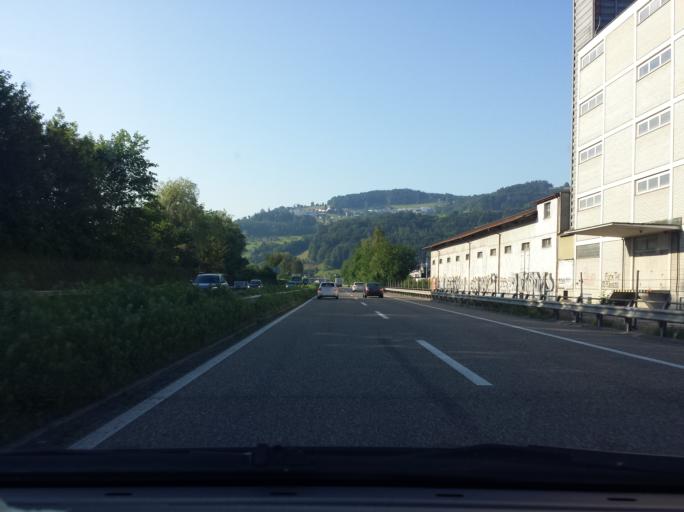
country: CH
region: Saint Gallen
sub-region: Wahlkreis Rheintal
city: Rheineck
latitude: 47.4714
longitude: 9.5887
